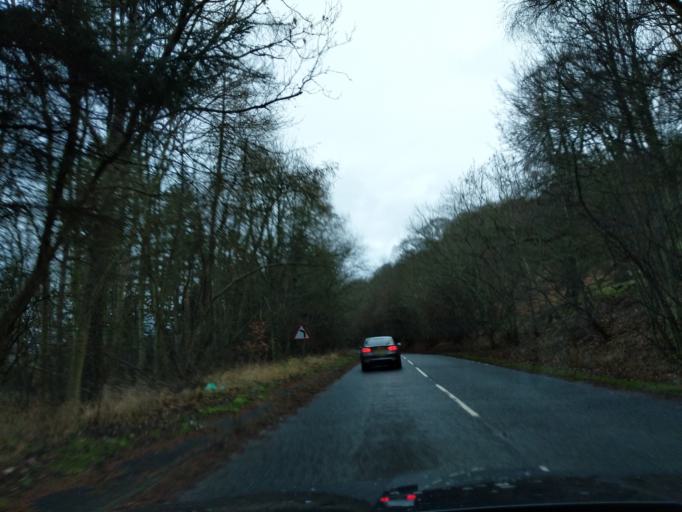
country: GB
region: Scotland
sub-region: The Scottish Borders
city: Galashiels
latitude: 55.6397
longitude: -2.8303
